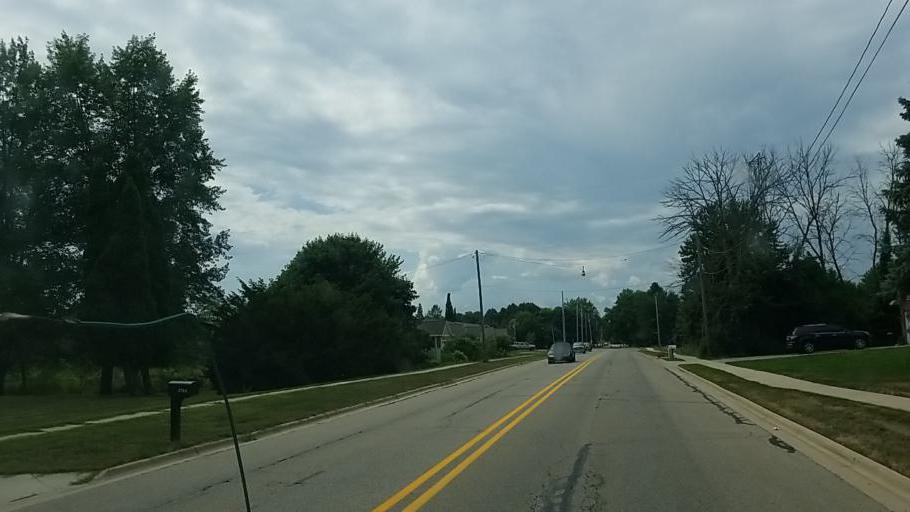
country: US
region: Michigan
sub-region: Kent County
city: Walker
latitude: 43.0013
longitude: -85.7618
